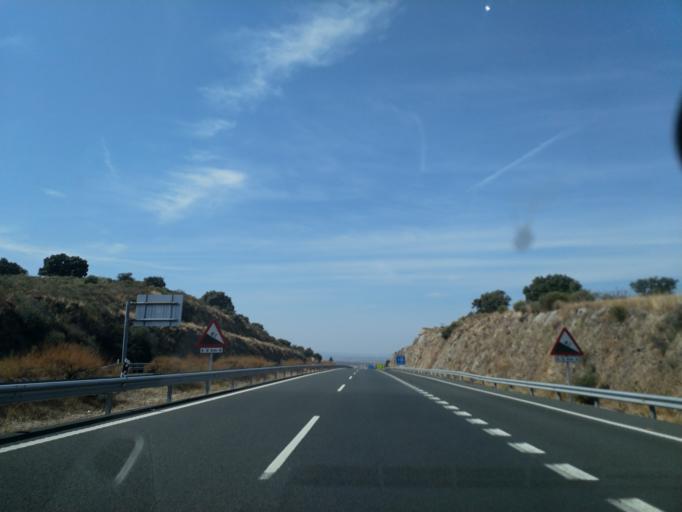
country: ES
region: Extremadura
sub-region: Provincia de Caceres
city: Navalmoral de la Mata
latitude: 39.8736
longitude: -5.5574
